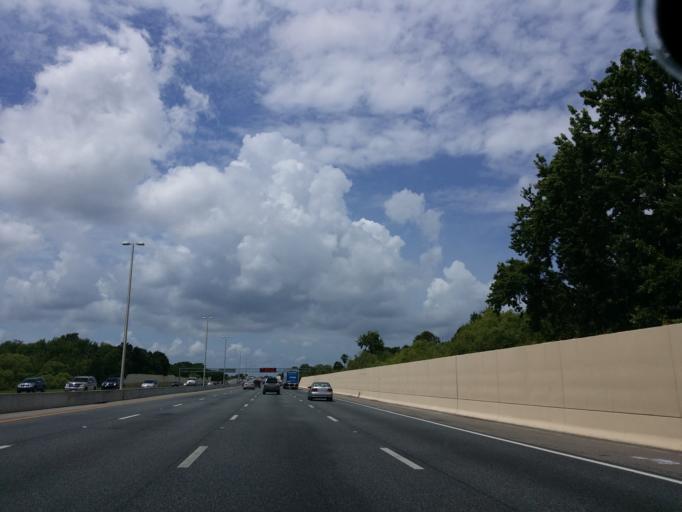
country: US
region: Florida
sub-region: Orange County
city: Winter Garden
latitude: 28.5453
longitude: -81.5990
